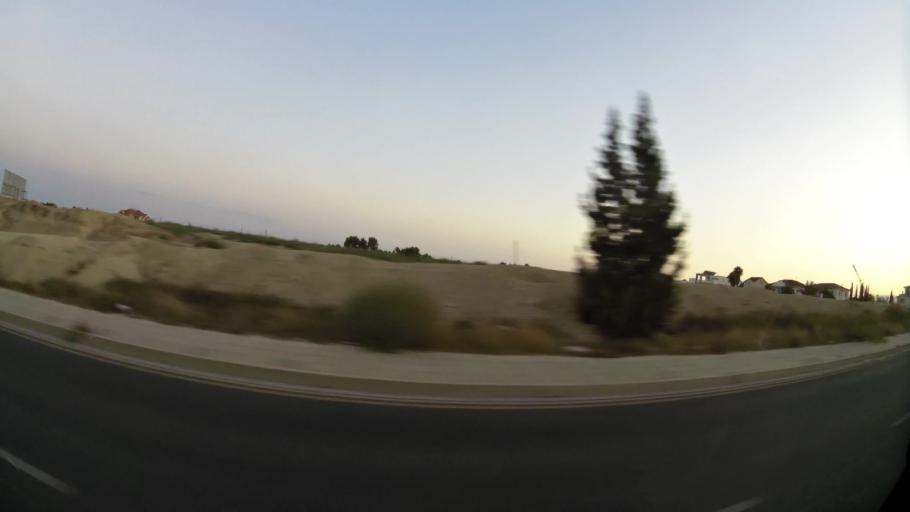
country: CY
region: Larnaka
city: Dhromolaxia
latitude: 34.9099
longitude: 33.5874
